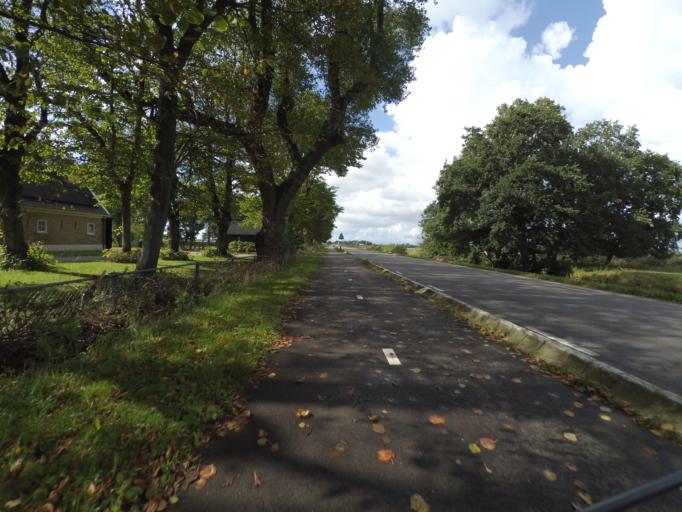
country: NL
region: North Holland
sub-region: Gemeente Schagen
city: Schagen
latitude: 52.8222
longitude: 4.7774
